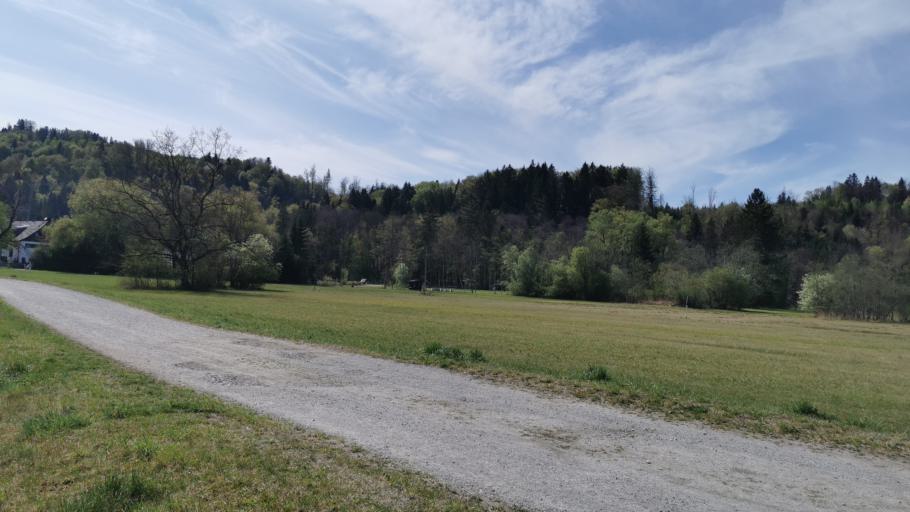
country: AT
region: Salzburg
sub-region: Politischer Bezirk Salzburg-Umgebung
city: Grodig
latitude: 47.7531
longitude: 12.9980
